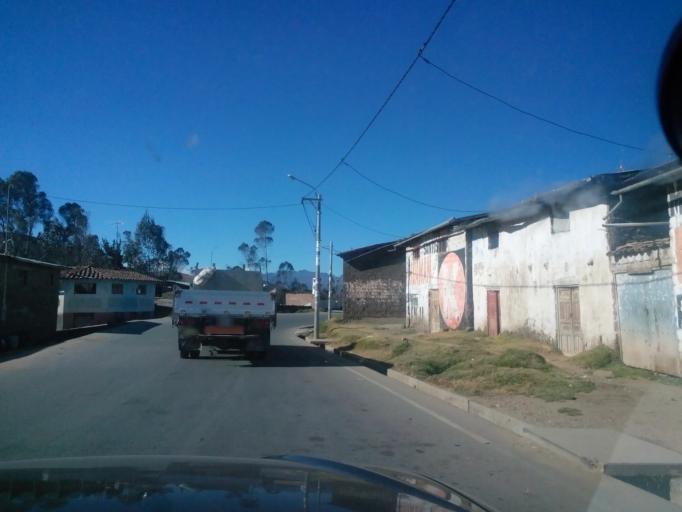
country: PE
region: Apurimac
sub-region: Provincia de Andahuaylas
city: Pacucha
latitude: -13.6511
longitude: -73.3022
